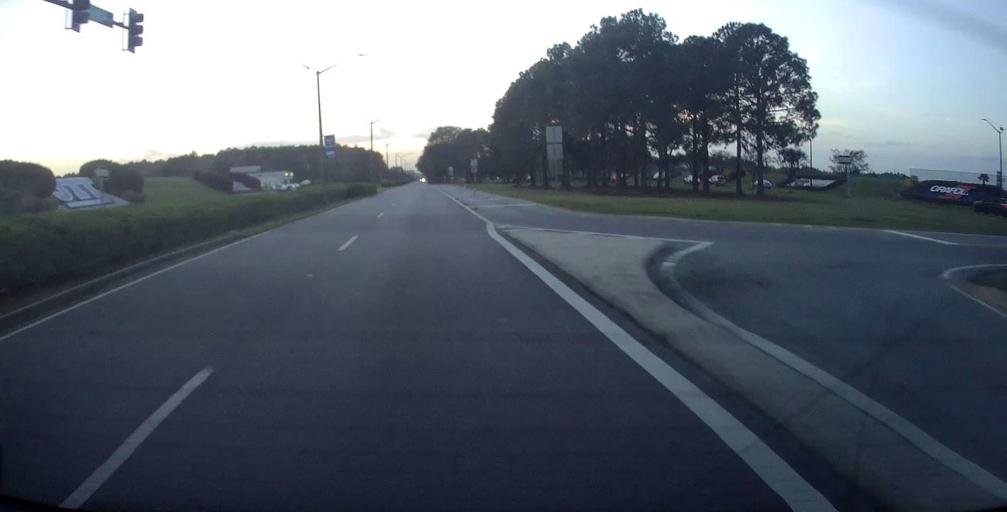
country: US
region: Georgia
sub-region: Chatham County
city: Pooler
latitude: 32.1377
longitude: -81.2232
